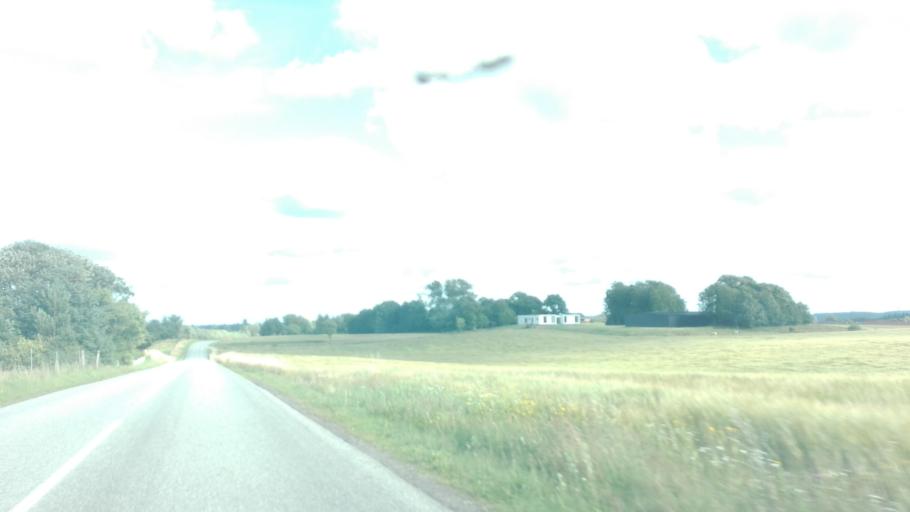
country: DK
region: Central Jutland
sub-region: Silkeborg Kommune
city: Virklund
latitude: 56.0890
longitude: 9.5611
